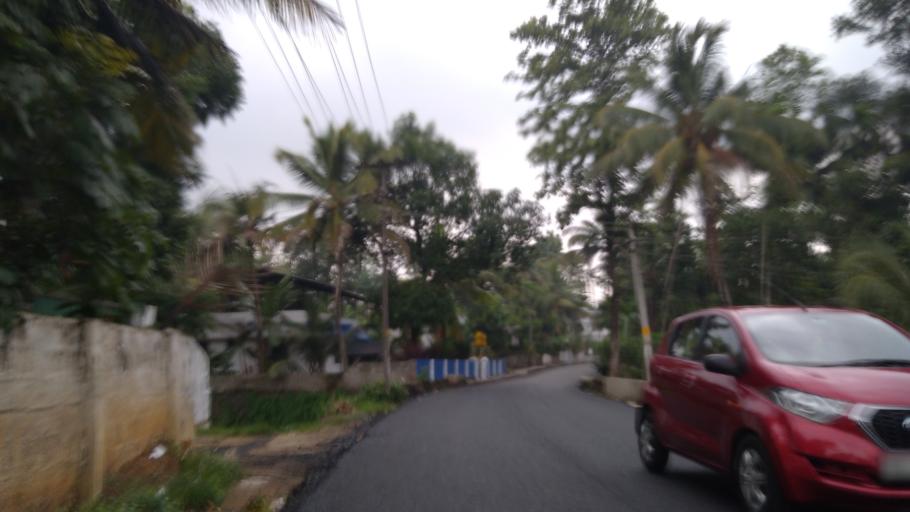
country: IN
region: Kerala
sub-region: Ernakulam
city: Perumbavoor
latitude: 10.0751
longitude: 76.5049
